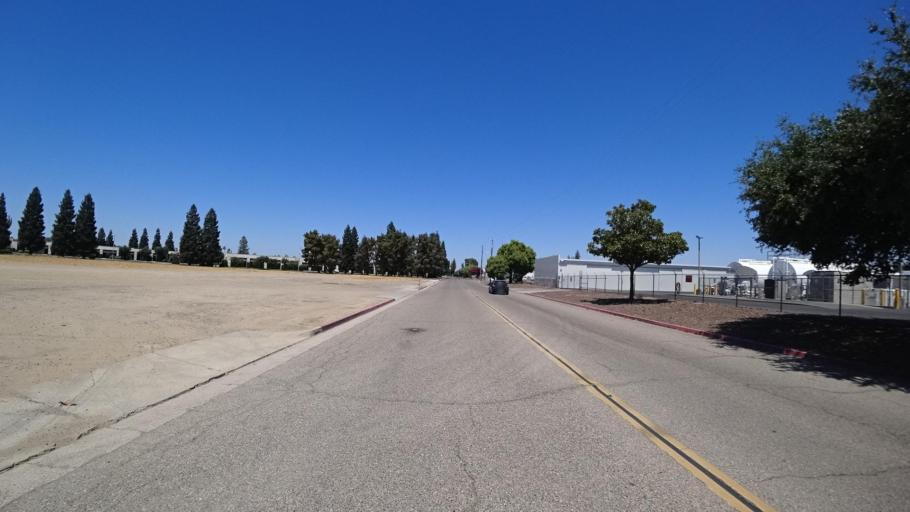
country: US
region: California
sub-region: Fresno County
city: Tarpey Village
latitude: 36.7749
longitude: -119.7267
